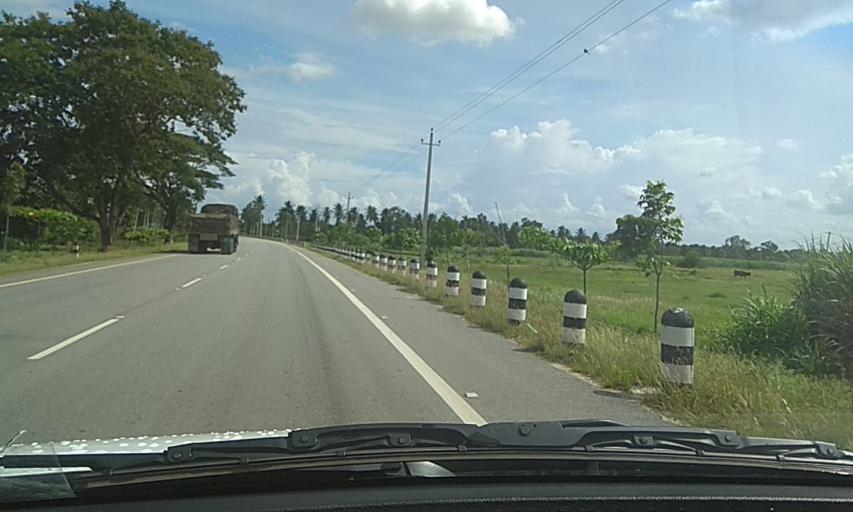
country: IN
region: Karnataka
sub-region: Mandya
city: Maddur
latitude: 12.6543
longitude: 77.0529
